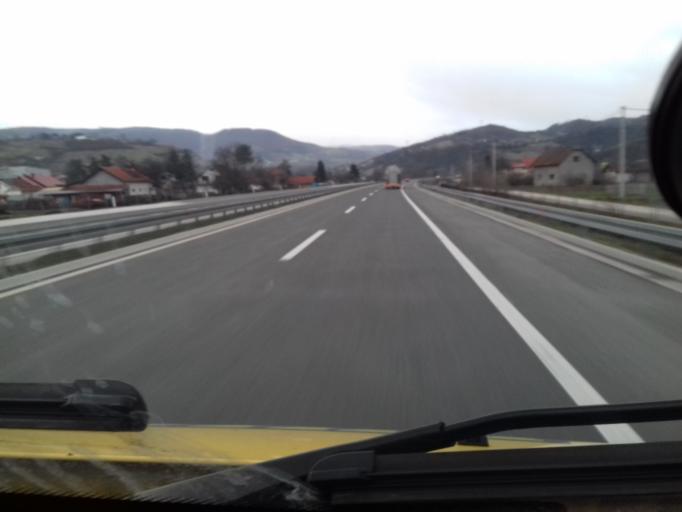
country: BA
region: Federation of Bosnia and Herzegovina
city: Ilijas
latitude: 43.9418
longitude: 18.2658
